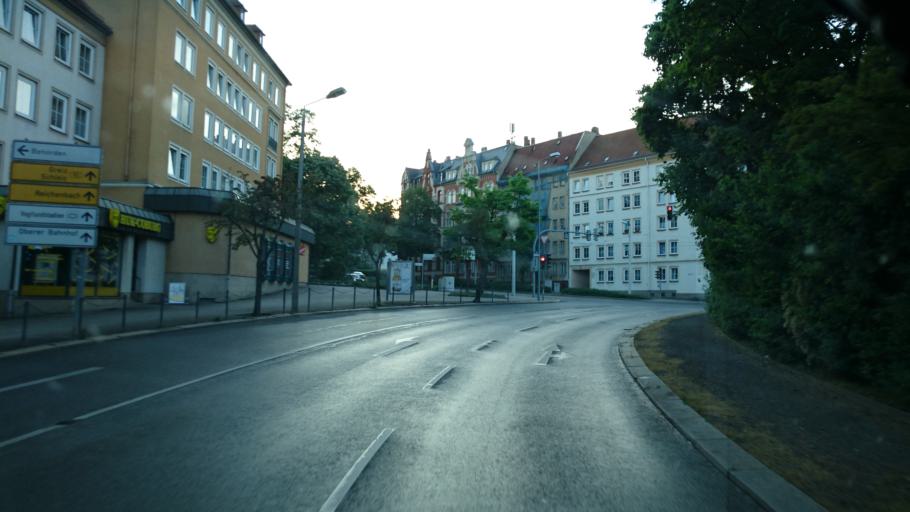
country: DE
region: Saxony
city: Plauen
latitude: 50.4949
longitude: 12.1240
